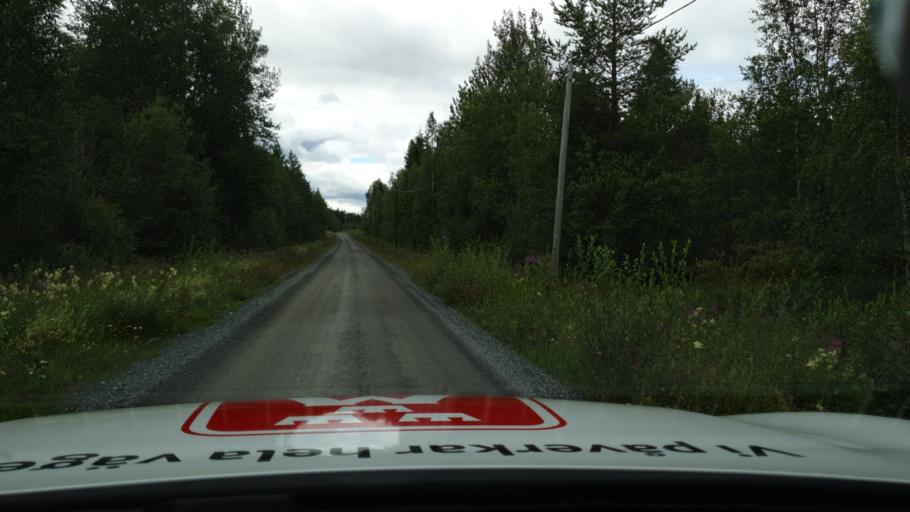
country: SE
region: Jaemtland
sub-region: Krokoms Kommun
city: Krokom
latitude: 63.3532
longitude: 14.3371
